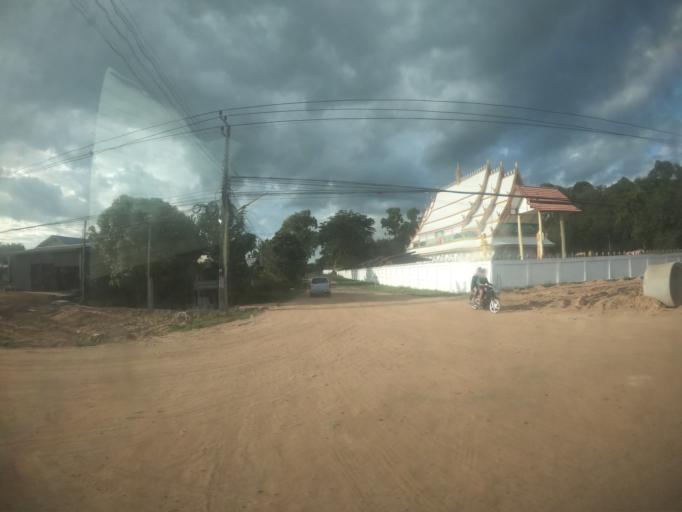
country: TH
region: Surin
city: Kap Choeng
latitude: 14.4548
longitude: 103.6845
